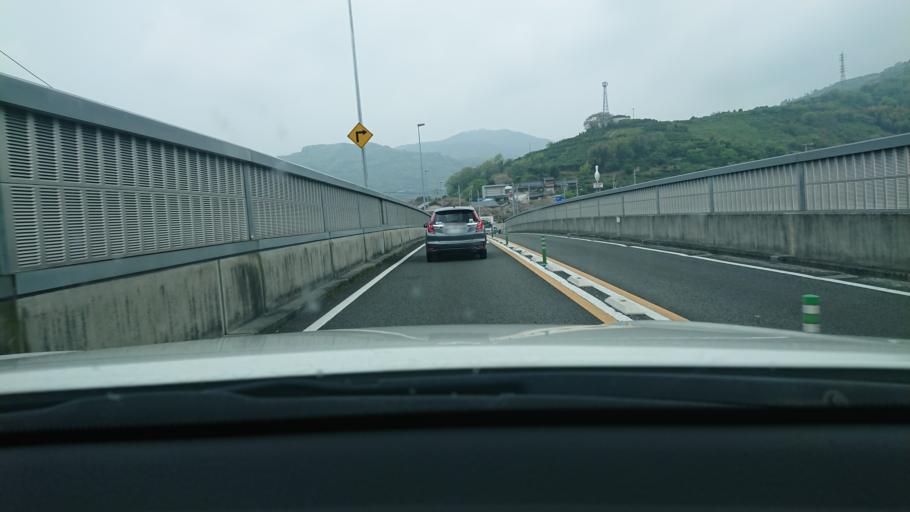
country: JP
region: Ehime
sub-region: Nishiuwa-gun
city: Ikata-cho
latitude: 33.4817
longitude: 132.4056
